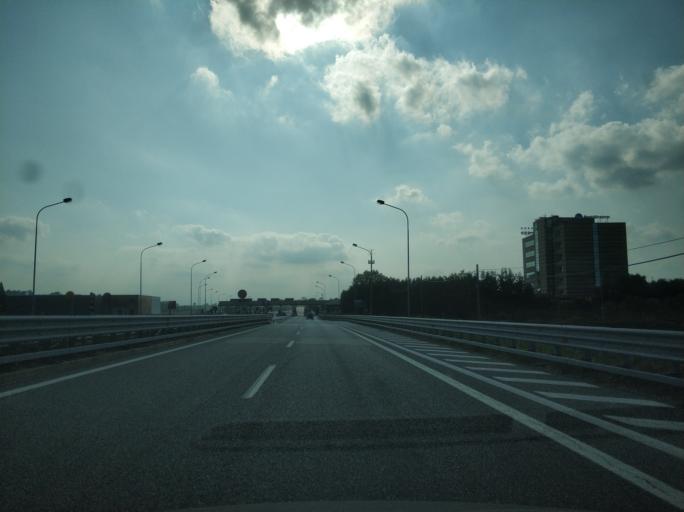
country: IT
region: Piedmont
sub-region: Provincia di Cuneo
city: Cervere
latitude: 44.6630
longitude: 7.7816
